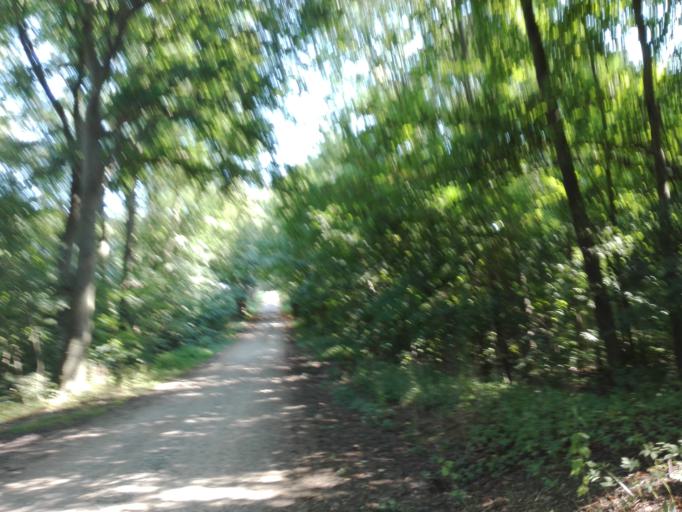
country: DK
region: Central Jutland
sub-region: Hedensted Kommune
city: Juelsminde
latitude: 55.7466
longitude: 10.0290
